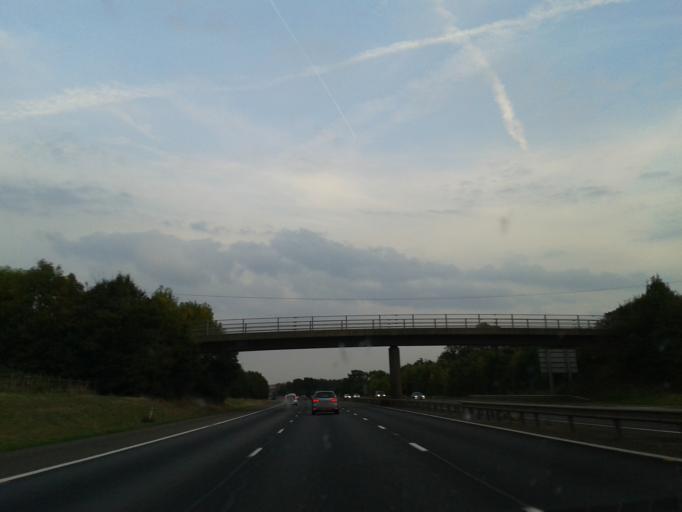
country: GB
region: England
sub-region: Warwickshire
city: Royal Leamington Spa
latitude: 52.2320
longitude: -1.5348
